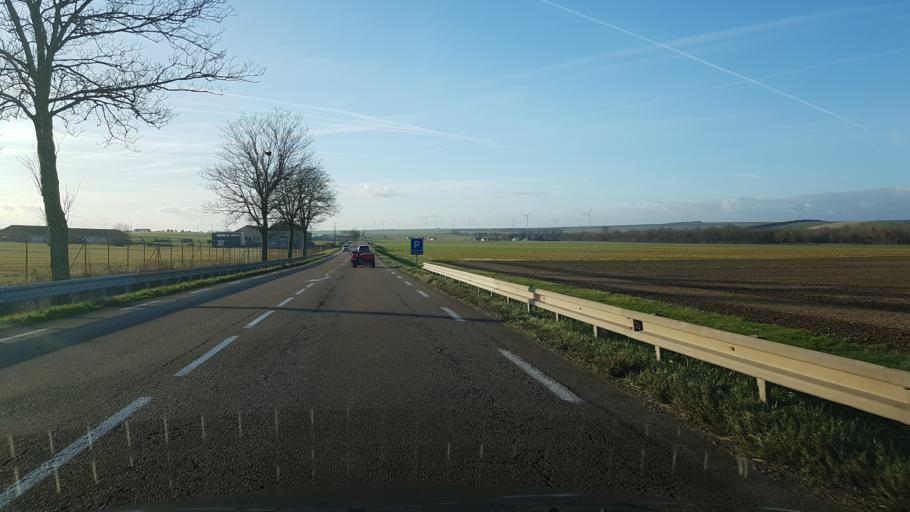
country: FR
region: Champagne-Ardenne
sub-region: Departement de la Marne
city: Vitry-le-Francois
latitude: 48.7438
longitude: 4.5191
